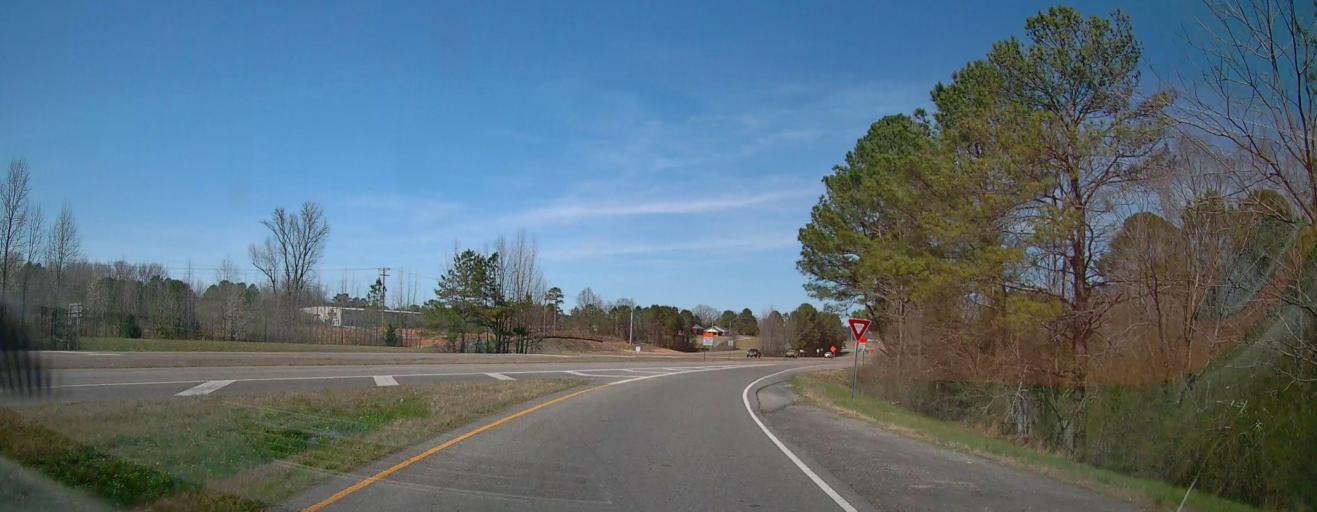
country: US
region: Alabama
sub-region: Cullman County
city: Cullman
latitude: 34.1844
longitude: -86.7846
